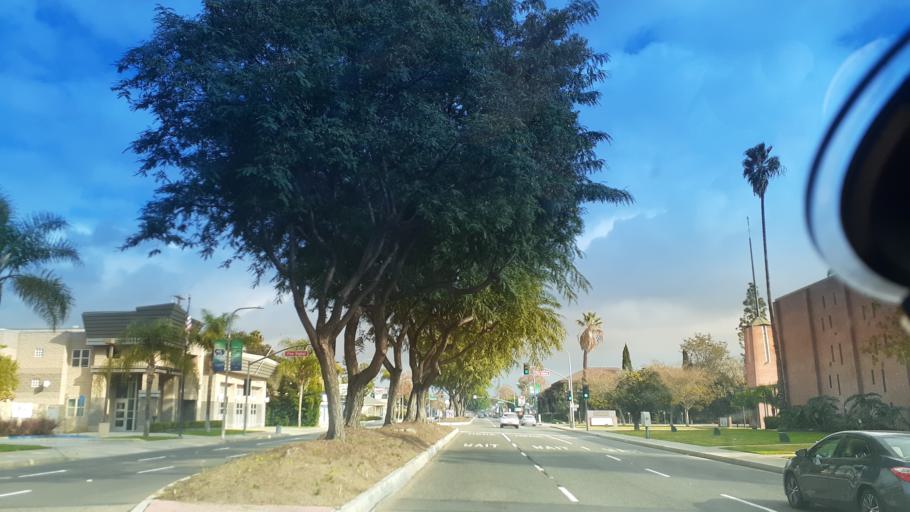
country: US
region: California
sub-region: Orange County
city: Santa Ana
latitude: 33.7601
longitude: -117.8789
